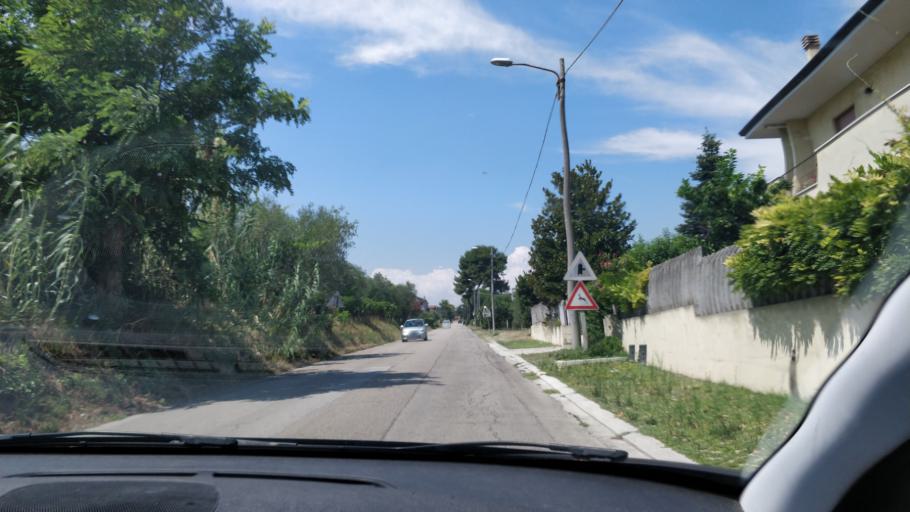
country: IT
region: Abruzzo
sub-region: Provincia di Chieti
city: Francavilla al Mare
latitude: 42.4228
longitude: 14.2637
